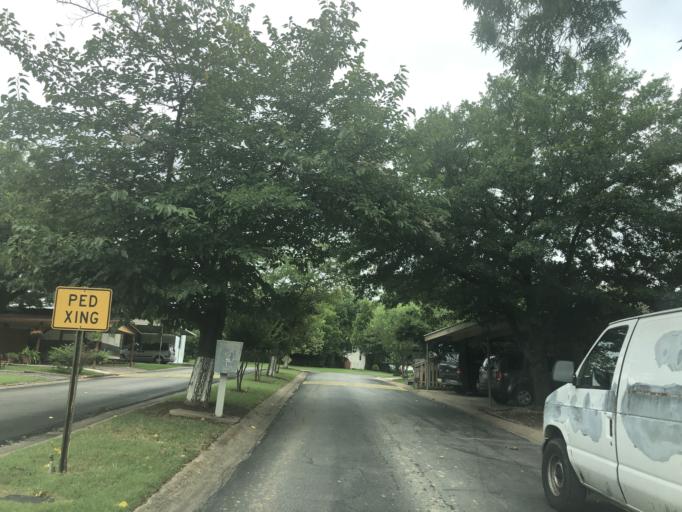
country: US
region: Texas
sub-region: Dallas County
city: Irving
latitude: 32.8084
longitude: -96.9959
